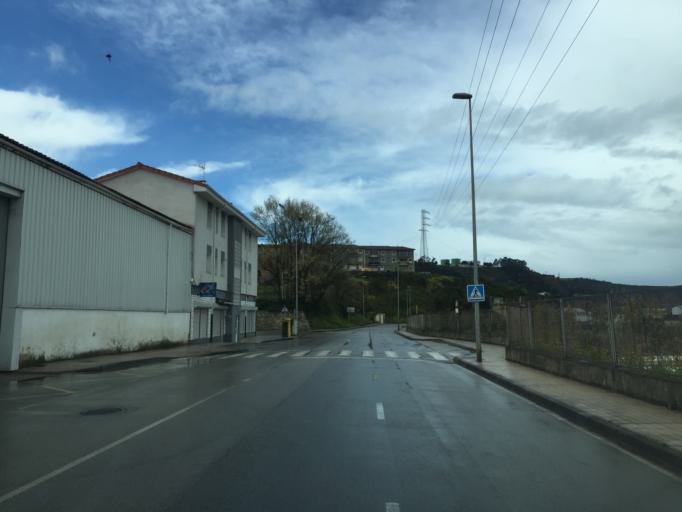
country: ES
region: Asturias
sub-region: Province of Asturias
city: Natahoyo
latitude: 43.5524
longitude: -5.7008
